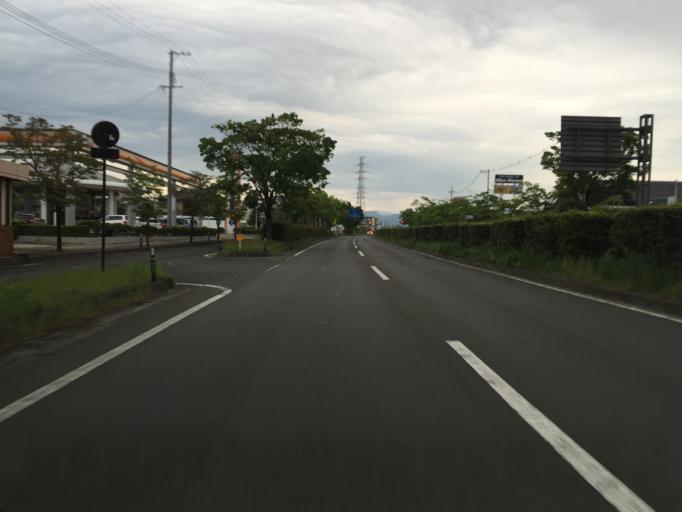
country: JP
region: Fukushima
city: Fukushima-shi
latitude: 37.7596
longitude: 140.4350
